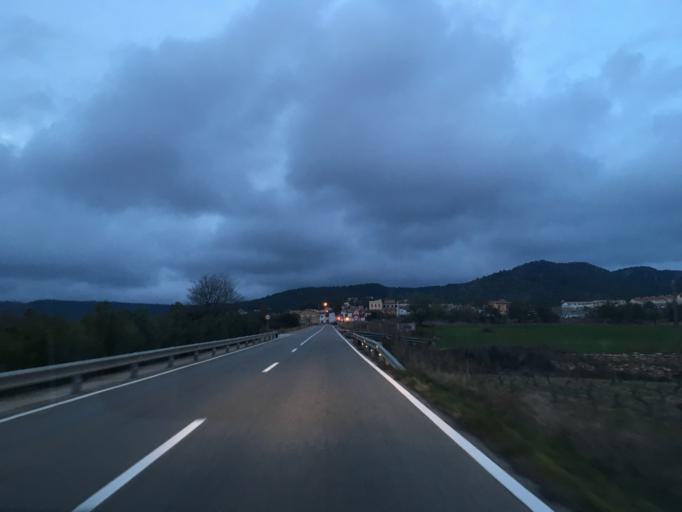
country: ES
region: Catalonia
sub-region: Provincia de Tarragona
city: la Bisbal del Penedes
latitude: 41.2879
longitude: 1.5252
